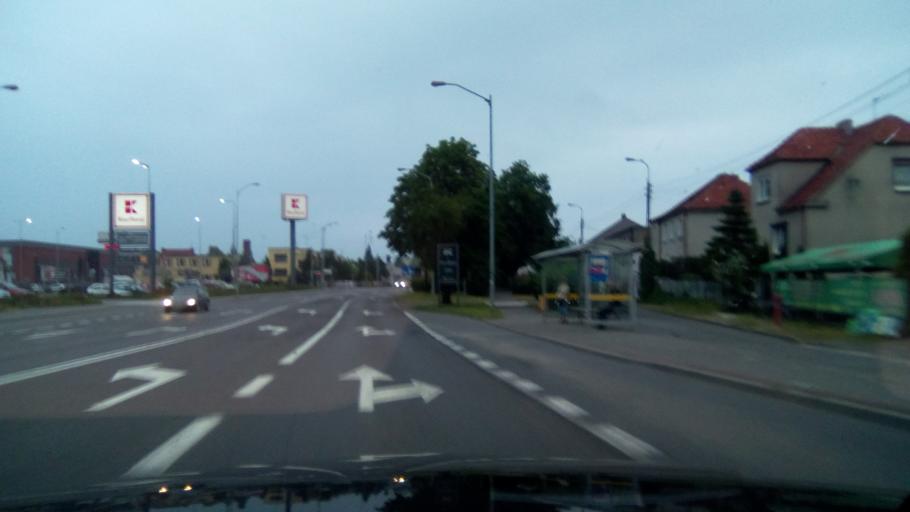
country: PL
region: Greater Poland Voivodeship
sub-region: Powiat poznanski
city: Swarzedz
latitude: 52.4081
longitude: 17.0845
